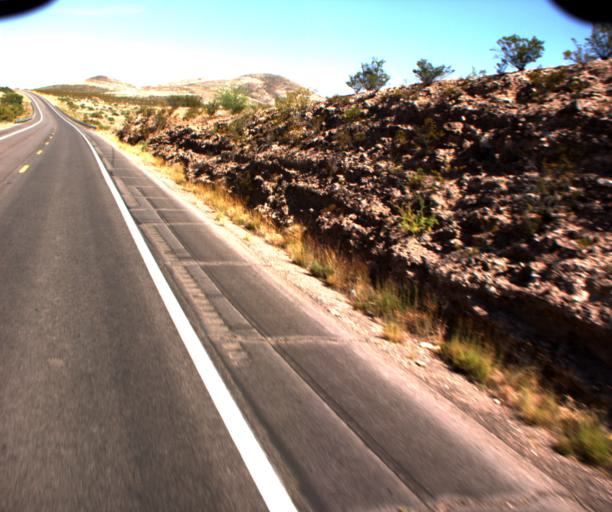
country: US
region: Arizona
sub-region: Greenlee County
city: Clifton
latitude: 32.7250
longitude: -109.1732
